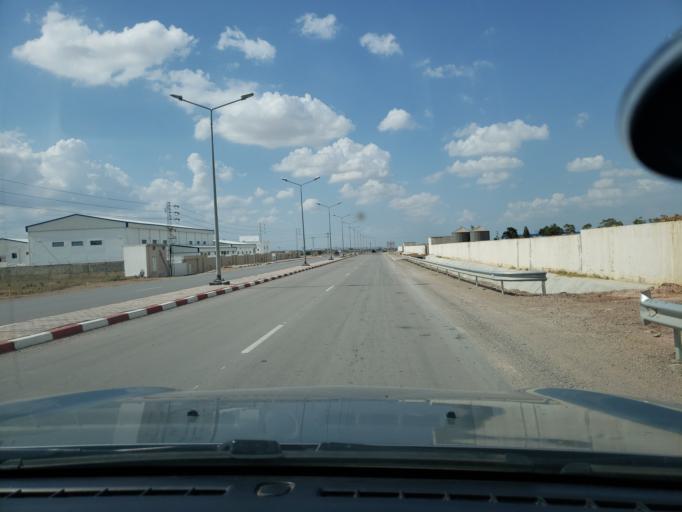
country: TN
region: Tunis
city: La Mohammedia
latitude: 36.5611
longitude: 10.0850
